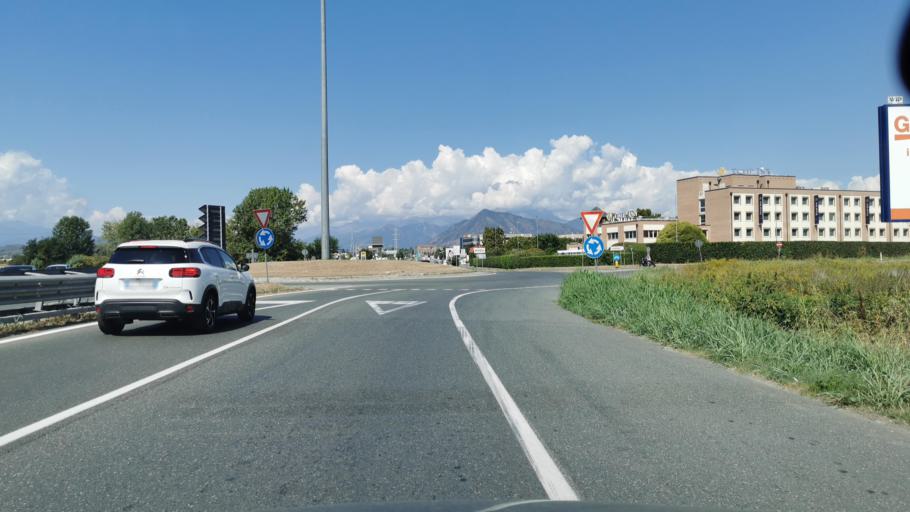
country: IT
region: Piedmont
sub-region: Provincia di Torino
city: Tetti Neirotti
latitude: 45.0566
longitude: 7.5610
